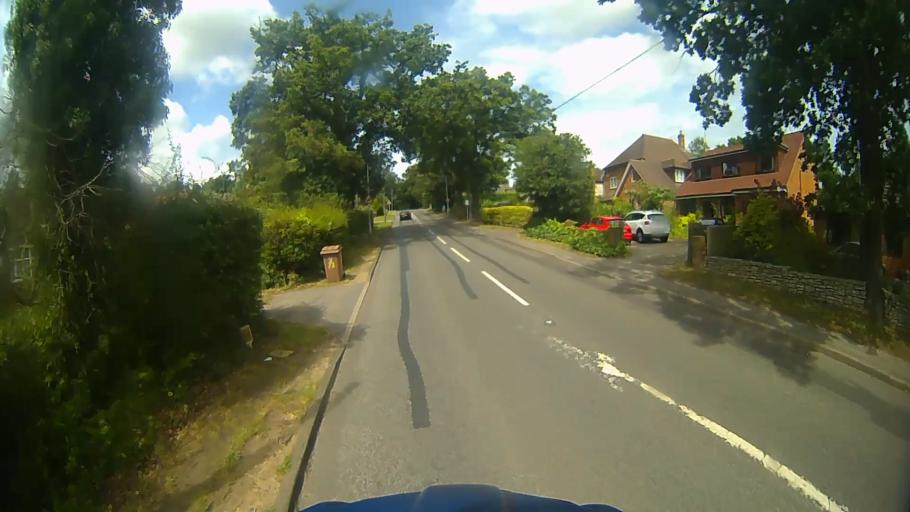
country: GB
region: England
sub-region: Wokingham
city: Barkham
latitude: 51.4030
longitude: -0.8756
